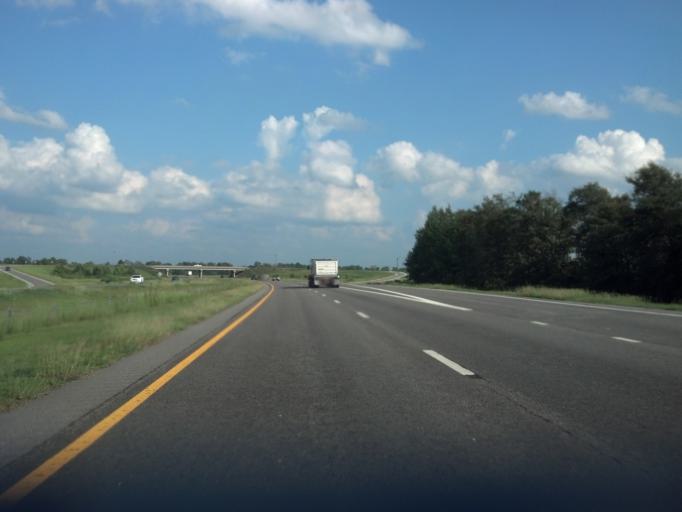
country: US
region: North Carolina
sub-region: Edgecombe County
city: Princeville
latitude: 35.8556
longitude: -77.4667
